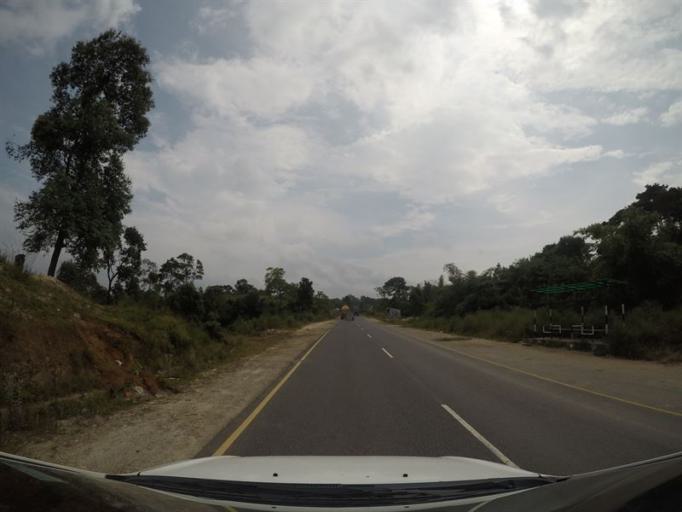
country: IN
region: Meghalaya
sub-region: East Khasi Hills
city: Shillong
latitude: 25.4872
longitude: 92.1917
